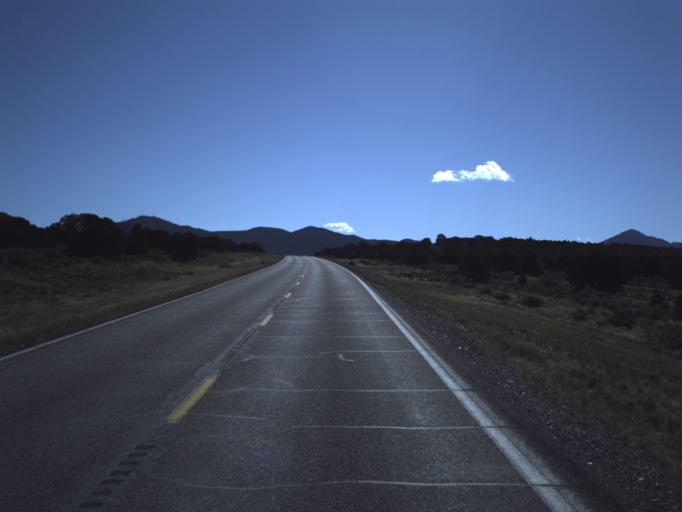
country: US
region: Utah
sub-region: Washington County
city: Enterprise
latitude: 37.6653
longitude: -113.4736
